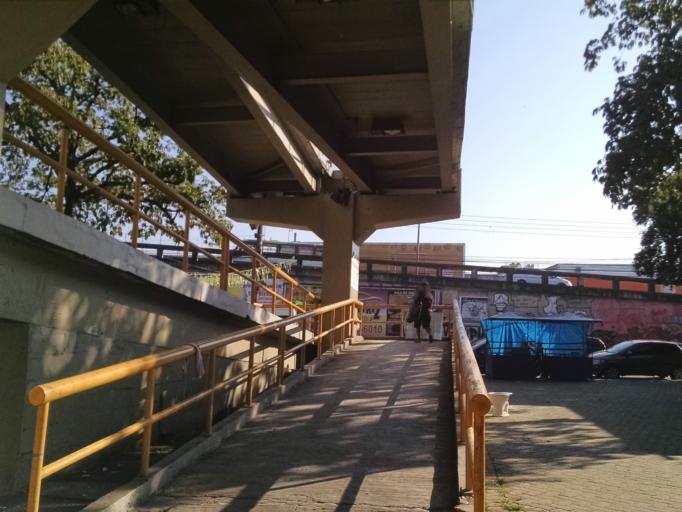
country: BR
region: Rio de Janeiro
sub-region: Sao Joao De Meriti
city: Sao Joao de Meriti
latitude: -22.8060
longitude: -43.3650
